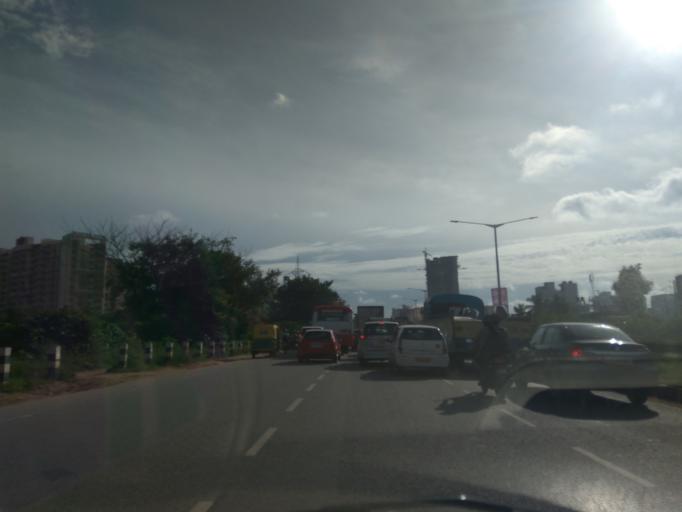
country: IN
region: Karnataka
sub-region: Bangalore Rural
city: Hoskote
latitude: 13.0146
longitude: 77.7006
